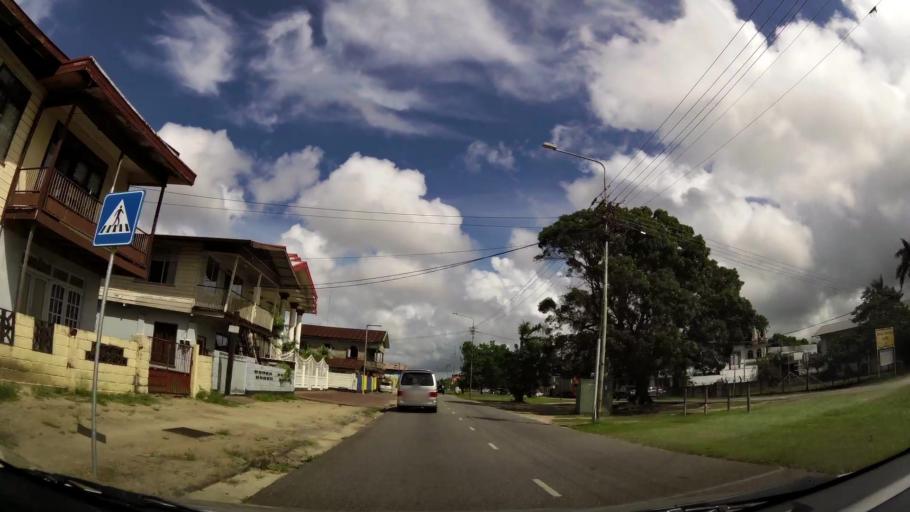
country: SR
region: Paramaribo
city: Paramaribo
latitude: 5.8298
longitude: -55.1713
